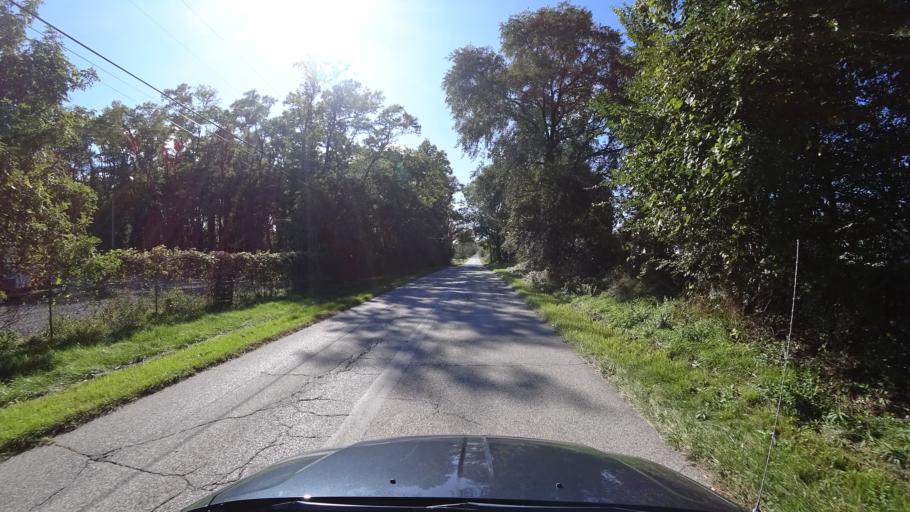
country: US
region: Indiana
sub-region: LaPorte County
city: Michigan City
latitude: 41.6781
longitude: -86.9133
